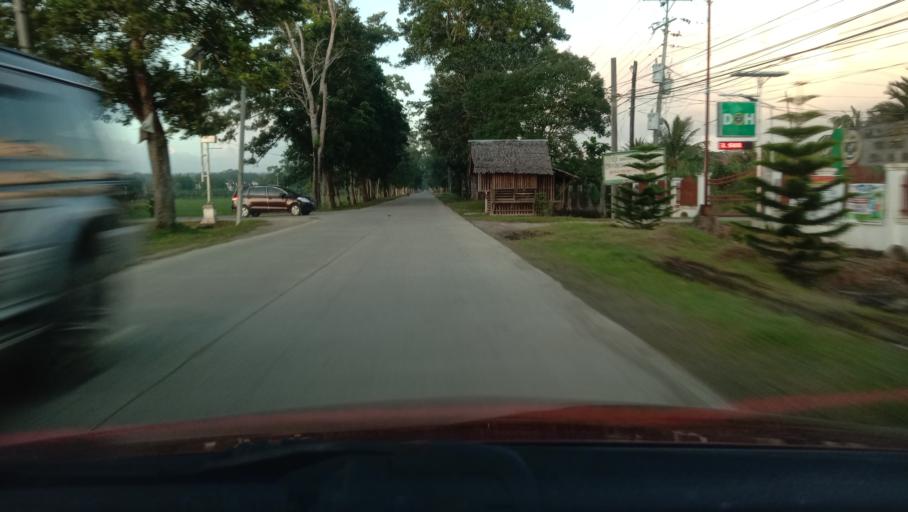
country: PH
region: Caraga
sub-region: Province of Agusan del Sur
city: Patin-ay
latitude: 8.5476
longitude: 125.9422
